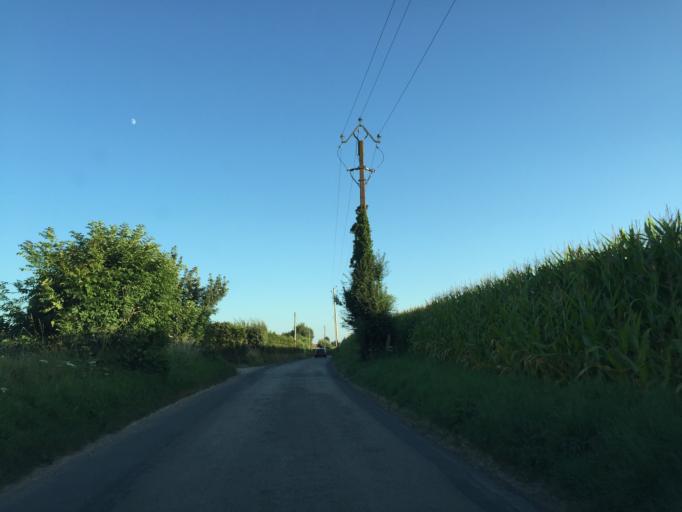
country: FR
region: Lower Normandy
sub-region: Departement du Calvados
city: Equemauville
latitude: 49.4008
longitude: 0.2052
